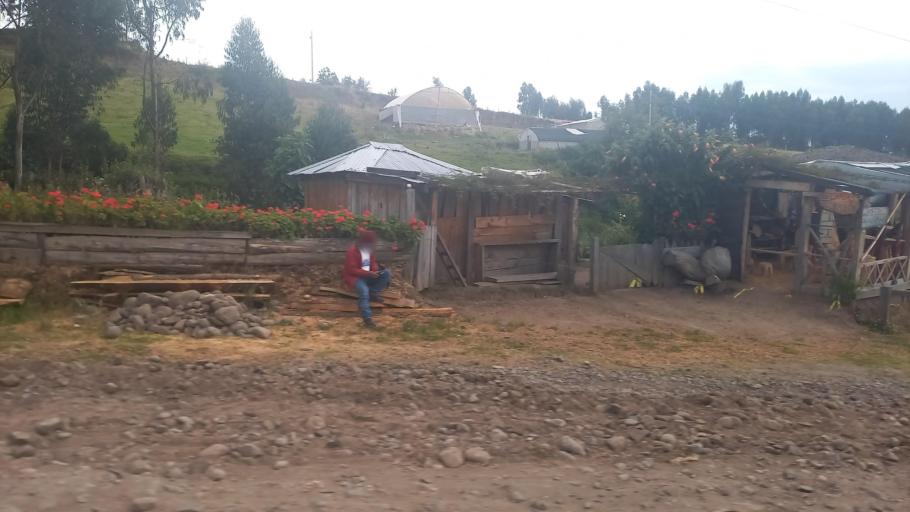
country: EC
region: Pichincha
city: Cayambe
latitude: 0.0914
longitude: -78.0959
